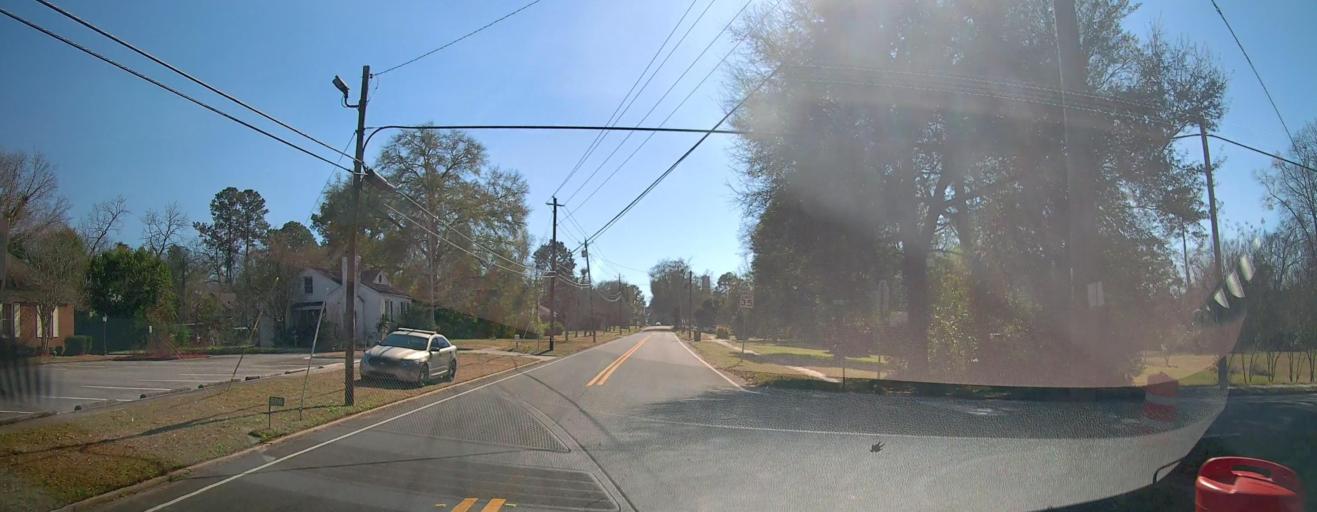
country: US
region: Georgia
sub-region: Macon County
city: Montezuma
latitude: 32.3093
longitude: -84.0257
